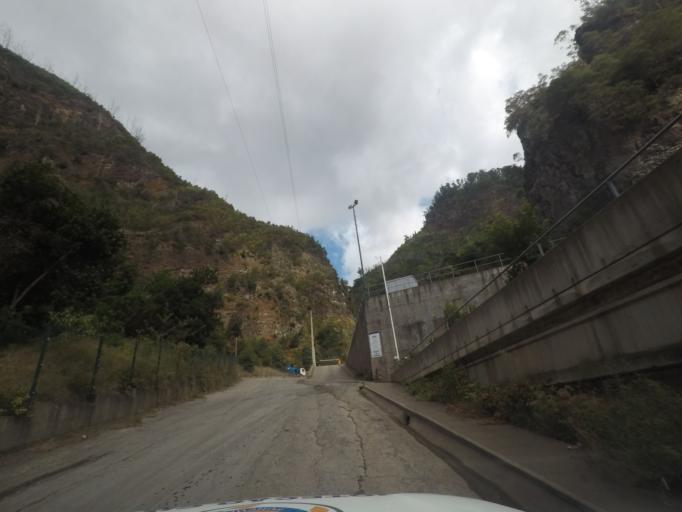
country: PT
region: Madeira
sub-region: Funchal
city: Nossa Senhora do Monte
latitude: 32.6844
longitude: -16.9152
